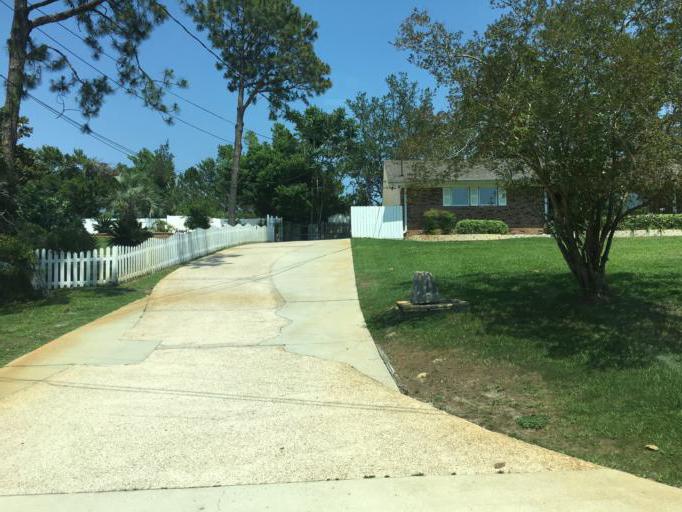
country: US
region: Florida
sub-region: Bay County
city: Laguna Beach
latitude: 30.2258
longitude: -85.8808
